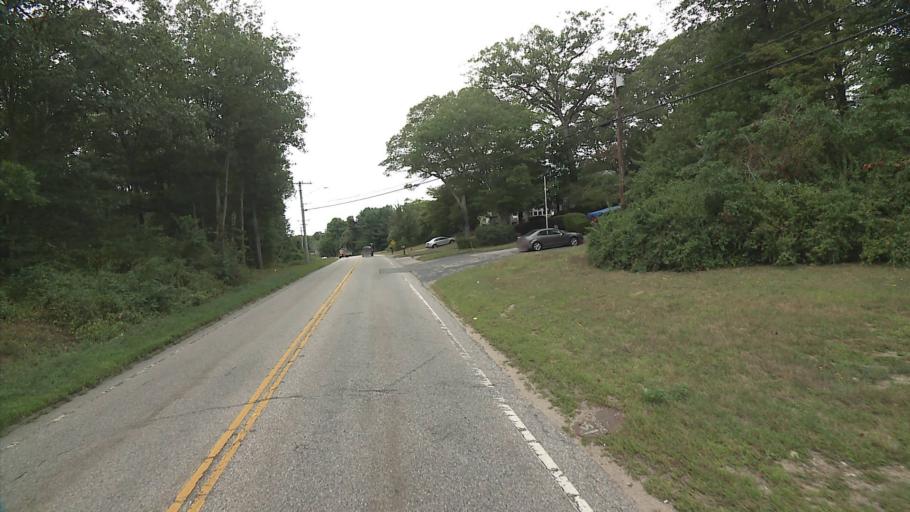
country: US
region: Connecticut
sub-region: New London County
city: Central Waterford
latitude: 41.3358
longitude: -72.1520
